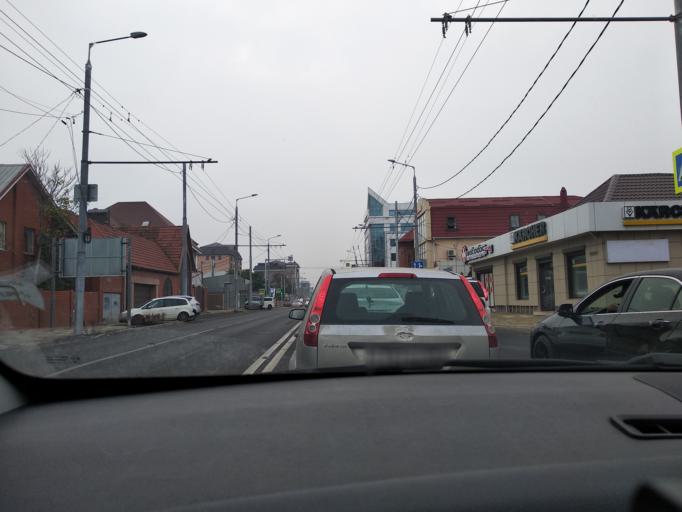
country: RU
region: Krasnodarskiy
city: Krasnodar
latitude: 45.0503
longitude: 38.9587
